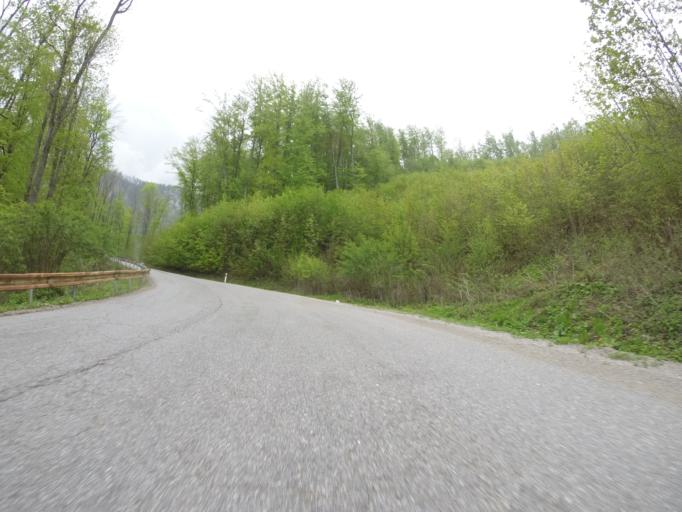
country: SK
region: Banskobystricky
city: Revuca
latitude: 48.7665
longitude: 20.0960
